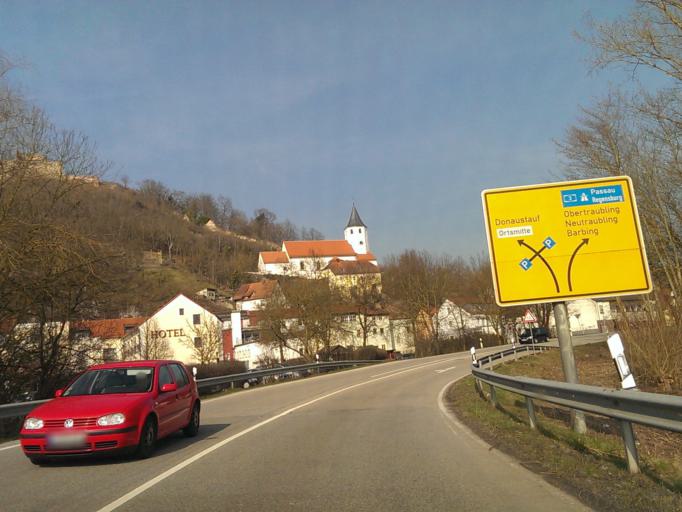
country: DE
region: Bavaria
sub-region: Upper Palatinate
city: Donaustauf
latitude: 49.0275
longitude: 12.2069
